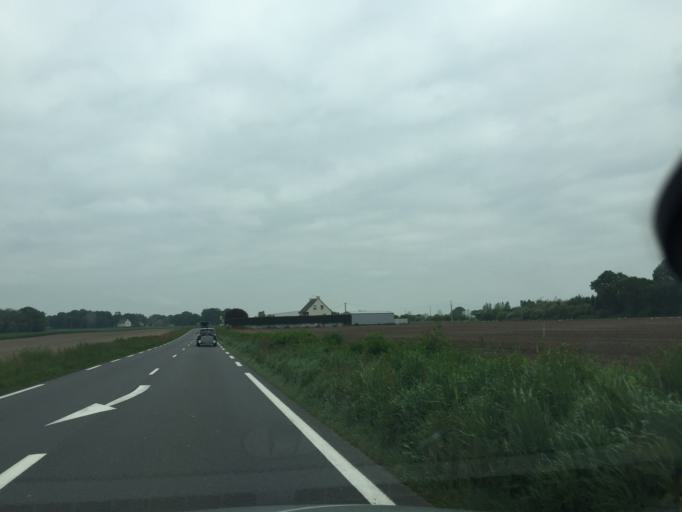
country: FR
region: Brittany
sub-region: Departement des Cotes-d'Armor
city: Henanbihen
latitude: 48.5264
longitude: -2.4256
